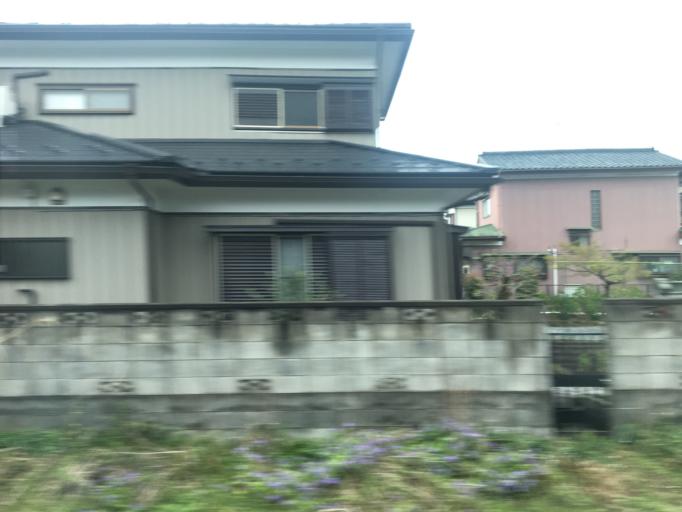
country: JP
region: Saitama
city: Ageoshimo
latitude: 35.9182
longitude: 139.5683
